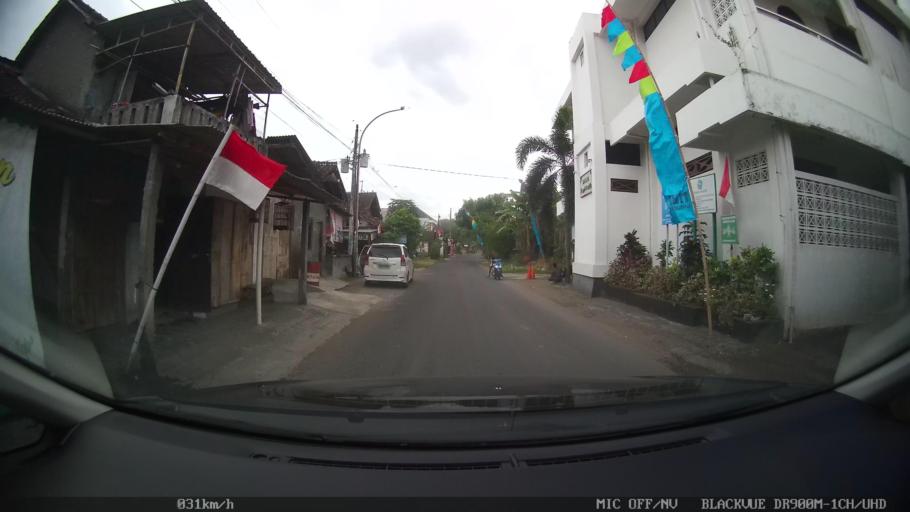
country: ID
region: Daerah Istimewa Yogyakarta
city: Sewon
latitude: -7.8730
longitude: 110.4163
